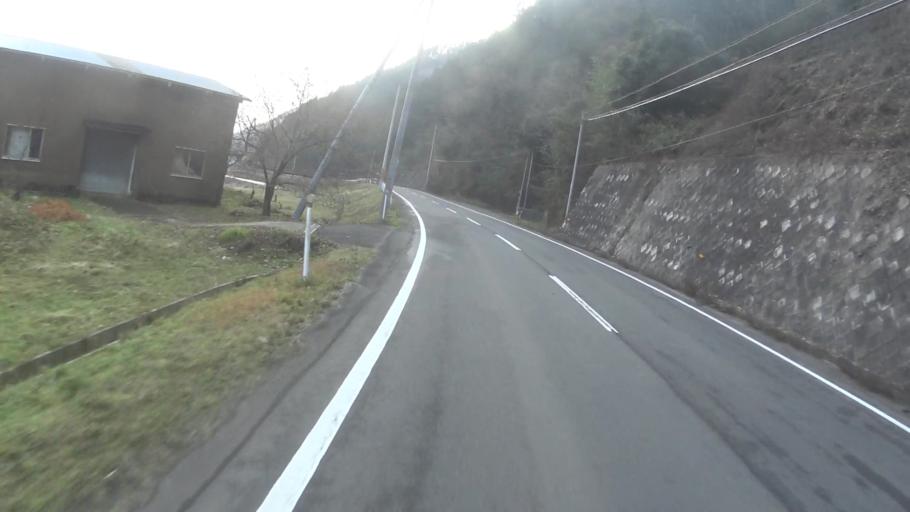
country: JP
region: Kyoto
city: Maizuru
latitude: 35.3956
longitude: 135.4132
